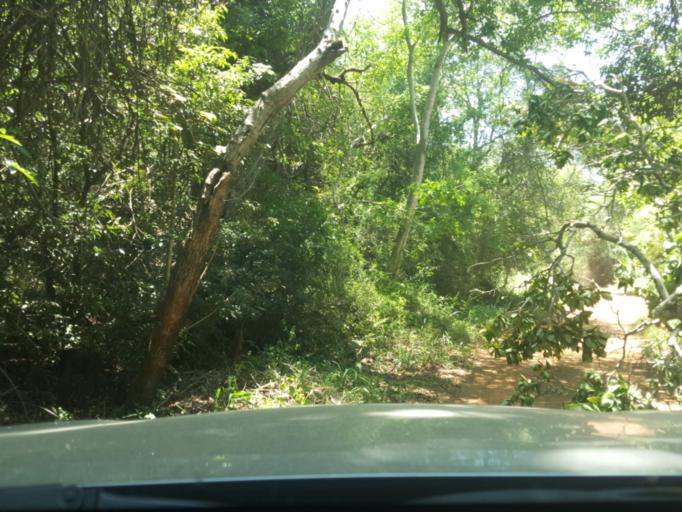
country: ZA
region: Limpopo
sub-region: Mopani District Municipality
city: Hoedspruit
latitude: -24.5944
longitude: 30.8269
